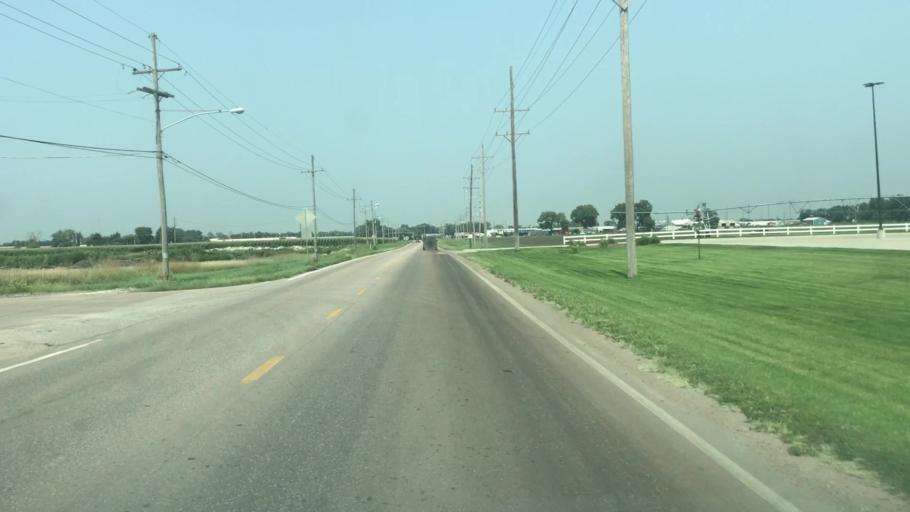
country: US
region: Nebraska
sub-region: Hall County
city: Grand Island
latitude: 40.9254
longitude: -98.3206
